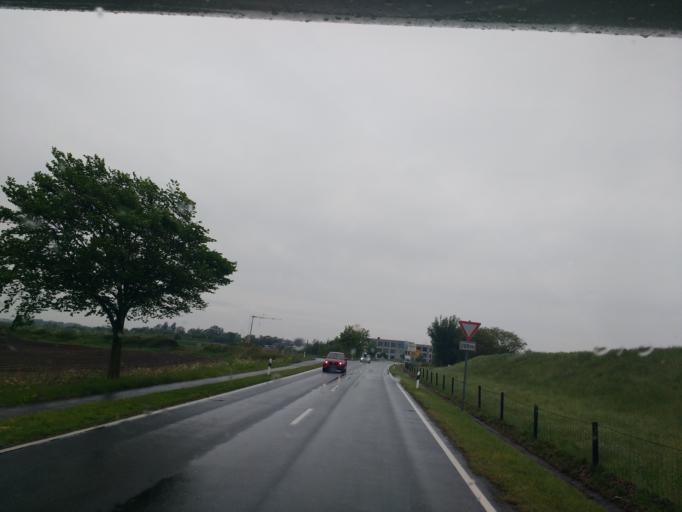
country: DE
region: Lower Saxony
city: Neuharlingersiel
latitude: 53.6963
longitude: 7.7253
